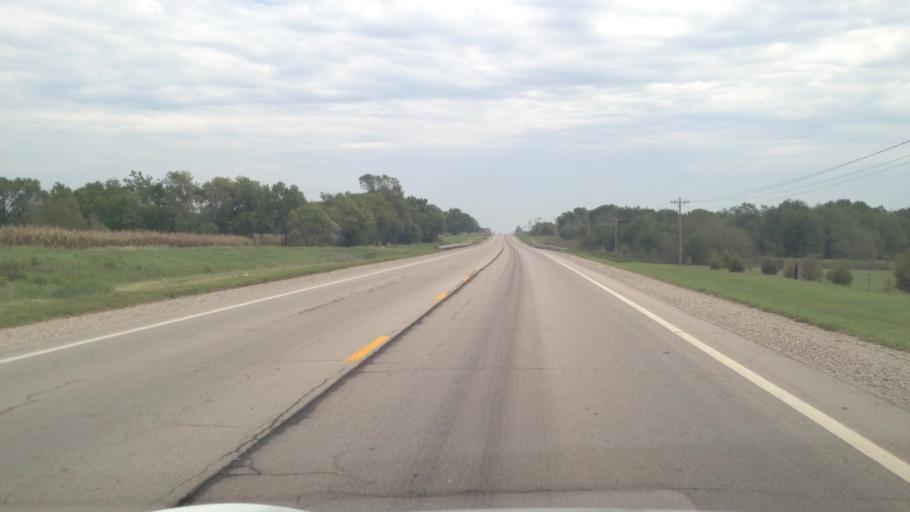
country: US
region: Kansas
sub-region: Crawford County
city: Girard
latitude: 37.5144
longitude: -94.9557
